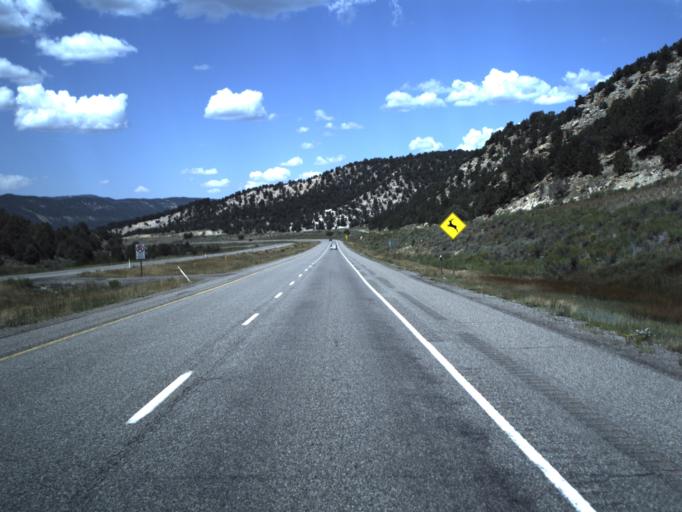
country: US
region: Utah
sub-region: Sevier County
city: Salina
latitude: 38.8424
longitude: -111.5383
